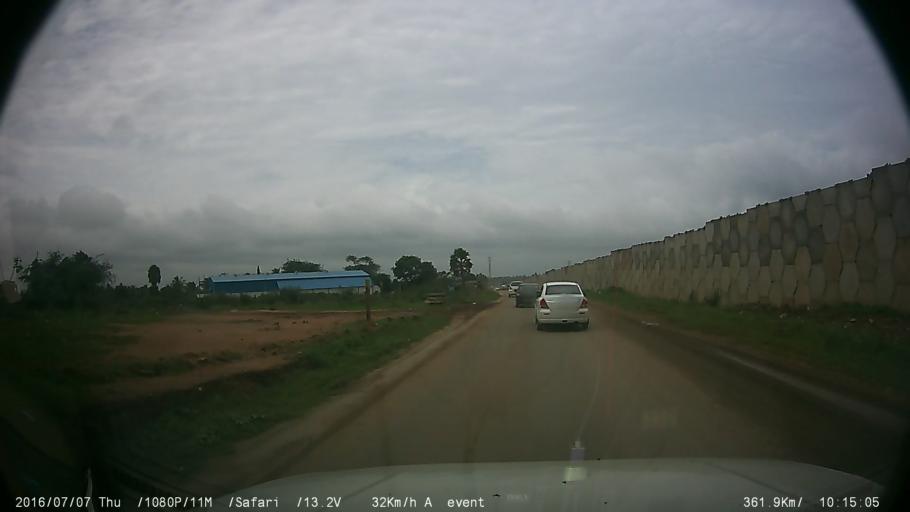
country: IN
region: Tamil Nadu
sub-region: Coimbatore
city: Madukkarai
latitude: 10.8825
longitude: 76.9100
